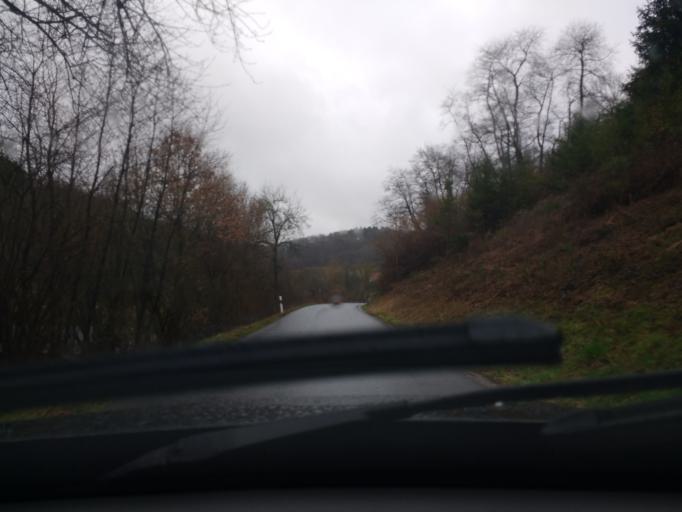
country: DE
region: Rheinland-Pfalz
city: Franzenheim
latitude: 49.6897
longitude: 6.6837
